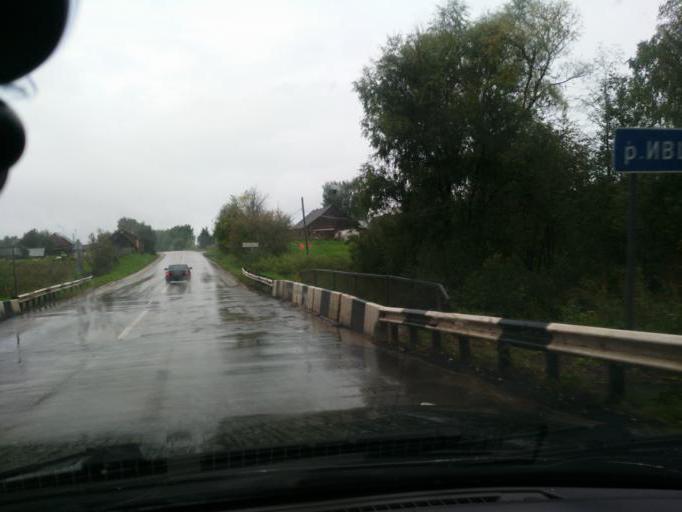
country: RU
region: Perm
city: Osa
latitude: 57.3724
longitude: 55.6094
